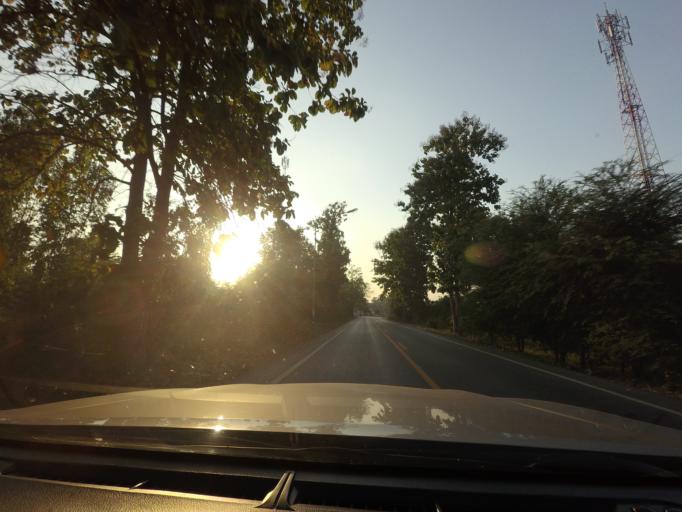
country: TH
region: Phitsanulok
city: Noen Maprang
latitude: 16.6890
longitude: 100.5331
